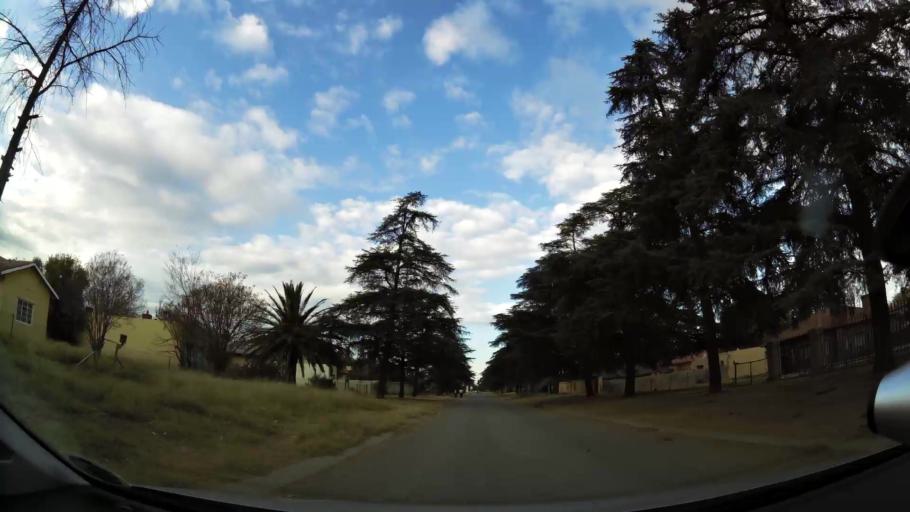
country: ZA
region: Orange Free State
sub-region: Lejweleputswa District Municipality
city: Welkom
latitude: -27.9917
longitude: 26.7085
